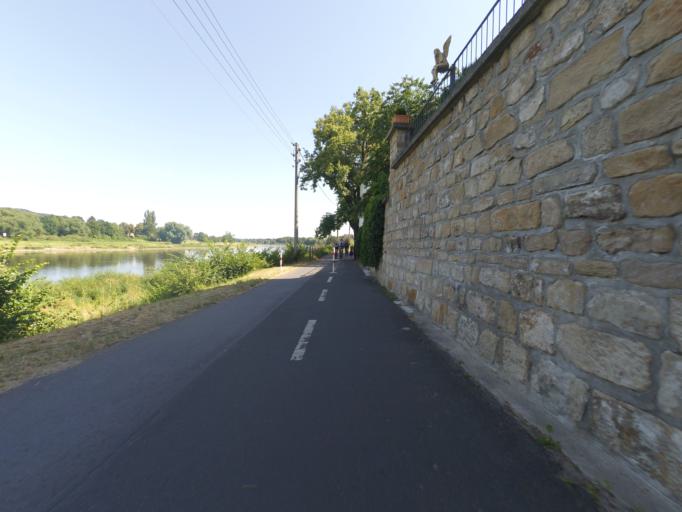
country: DE
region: Saxony
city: Heidenau
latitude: 51.0257
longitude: 13.8397
